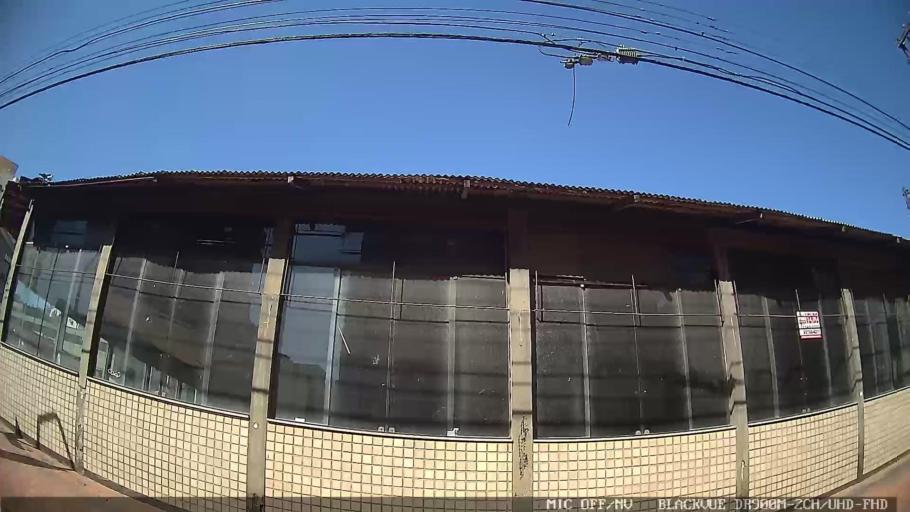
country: BR
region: Sao Paulo
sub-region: Guaruja
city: Guaruja
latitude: -23.9847
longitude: -46.2038
